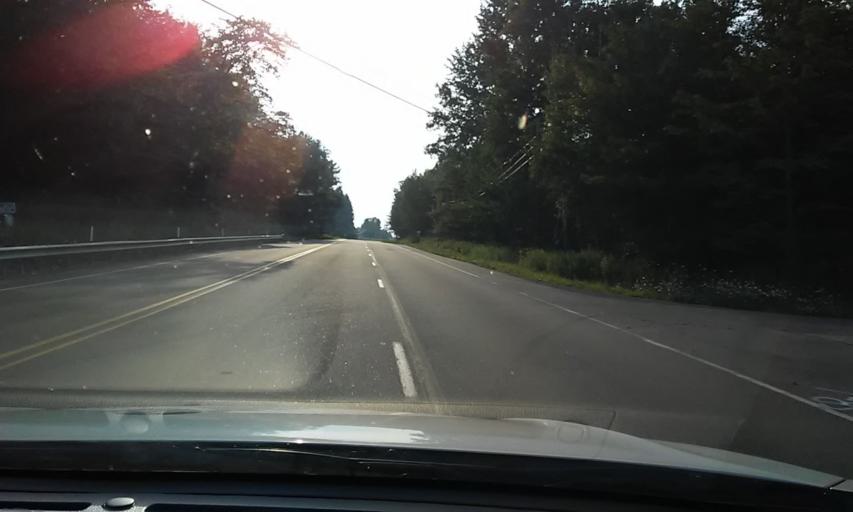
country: US
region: Pennsylvania
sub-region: McKean County
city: Smethport
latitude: 41.7238
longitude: -78.6195
